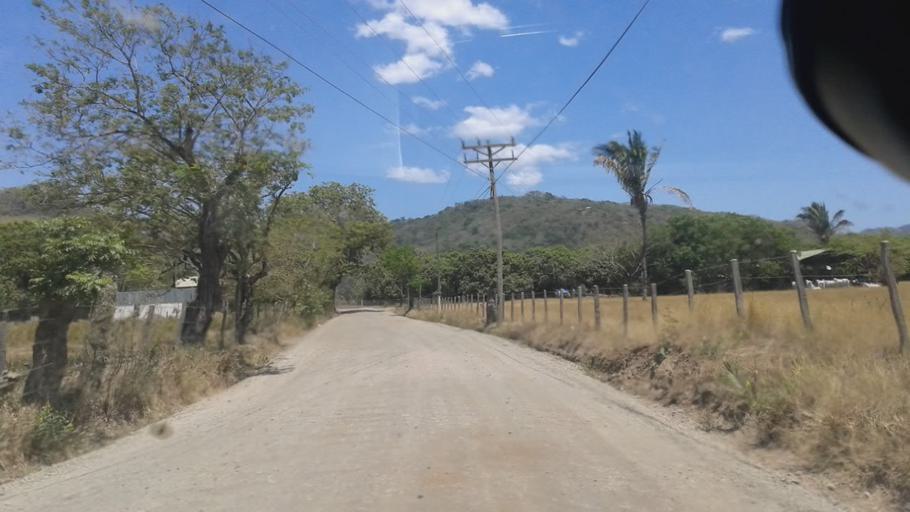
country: CR
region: Guanacaste
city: Samara
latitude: 9.9934
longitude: -85.6783
